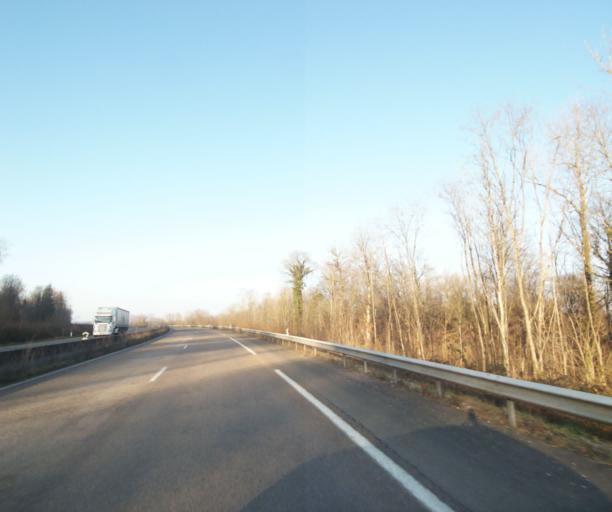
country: FR
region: Champagne-Ardenne
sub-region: Departement de la Haute-Marne
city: Chevillon
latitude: 48.5304
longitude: 5.0923
